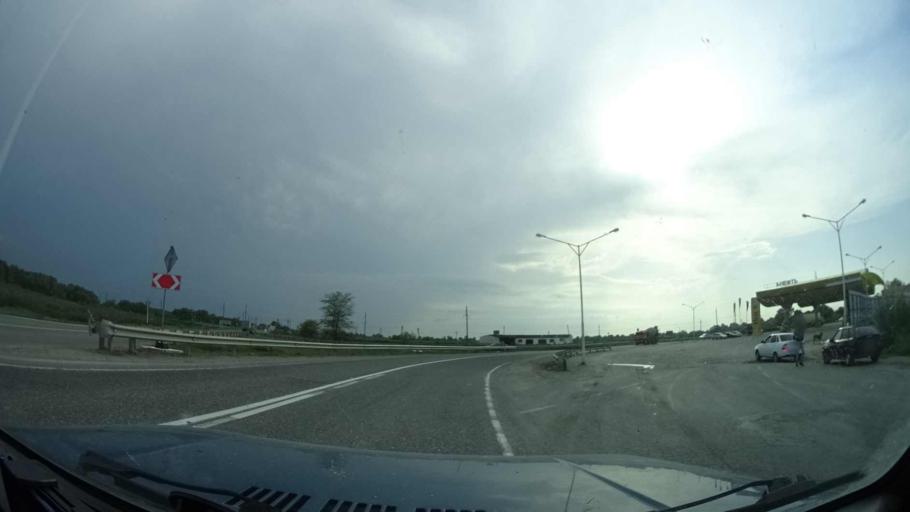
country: RU
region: Dagestan
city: Babayurt
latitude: 43.5740
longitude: 46.7360
